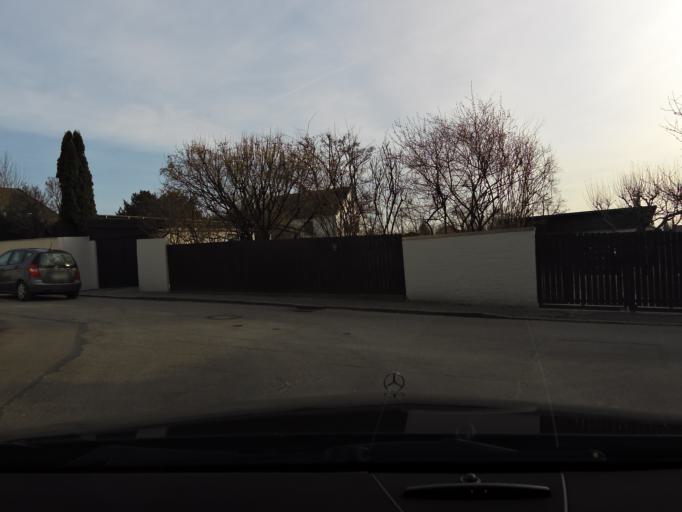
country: DE
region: Bavaria
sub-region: Lower Bavaria
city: Landshut
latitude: 48.5297
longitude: 12.1586
